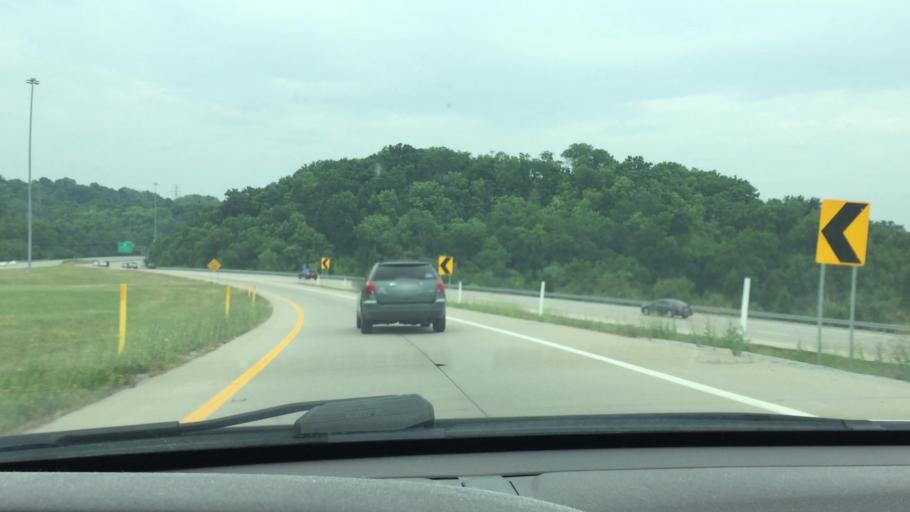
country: US
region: Kentucky
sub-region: Campbell County
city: Highland Heights
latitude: 39.0495
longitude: -84.4634
